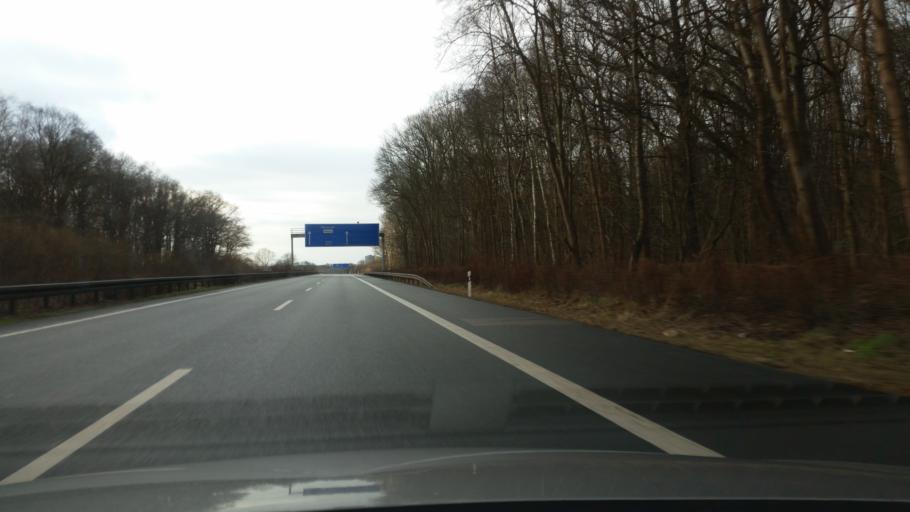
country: DE
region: Lower Saxony
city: Laatzen
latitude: 52.3052
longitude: 9.8484
